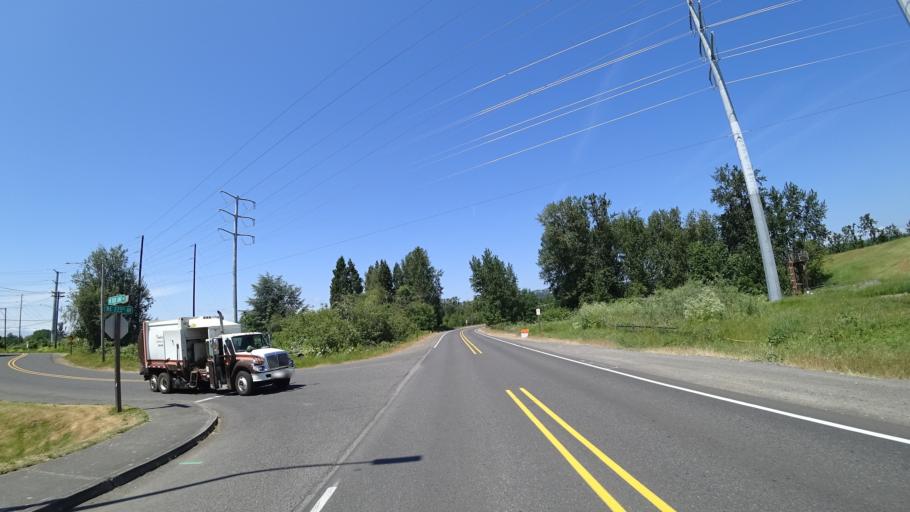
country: US
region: Oregon
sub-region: Multnomah County
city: Fairview
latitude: 45.5552
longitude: -122.4355
